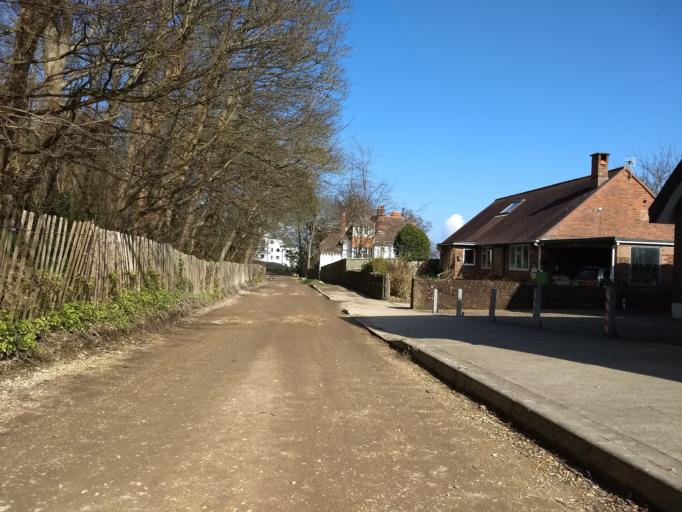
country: GB
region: England
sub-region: Isle of Wight
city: Seaview
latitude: 50.7155
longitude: -1.1074
